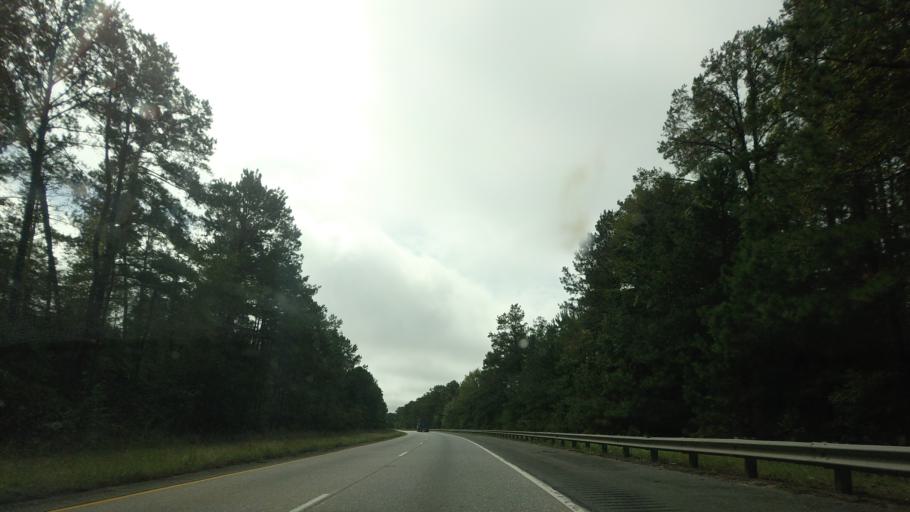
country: US
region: Georgia
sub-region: Bibb County
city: Macon
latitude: 32.7634
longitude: -83.5565
